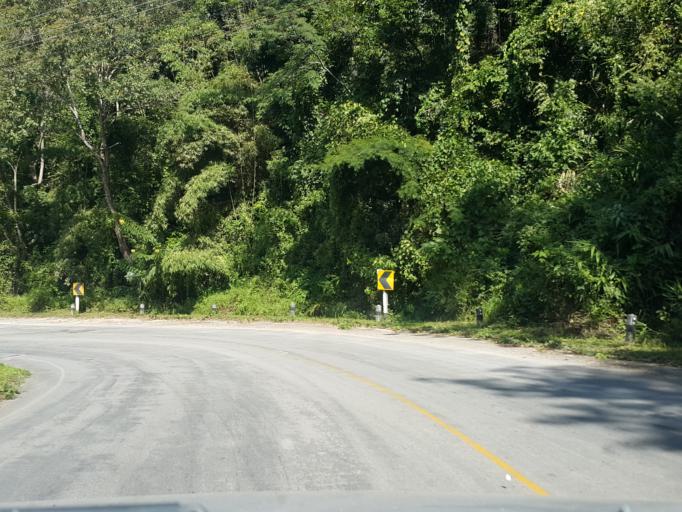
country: TH
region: Chiang Mai
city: Mae Taeng
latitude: 19.1246
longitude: 98.7609
